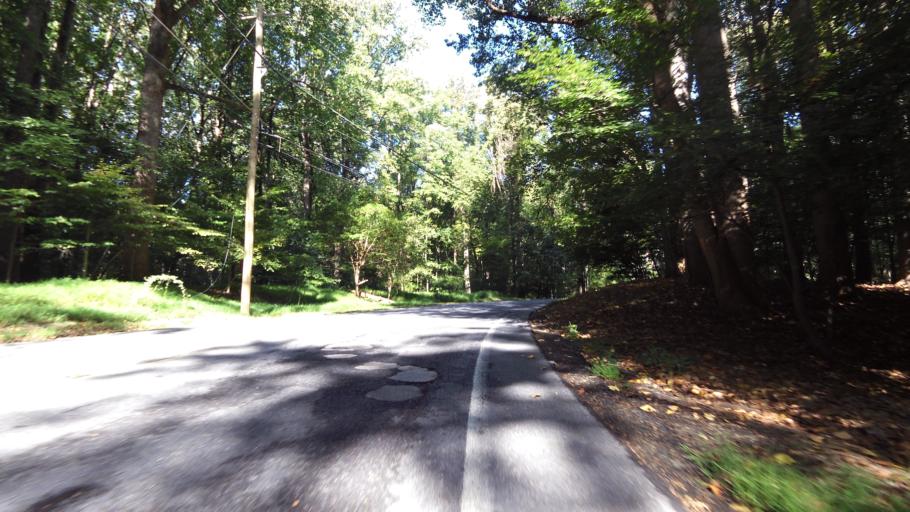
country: US
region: Maryland
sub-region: Montgomery County
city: Potomac
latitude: 38.9920
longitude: -77.2283
